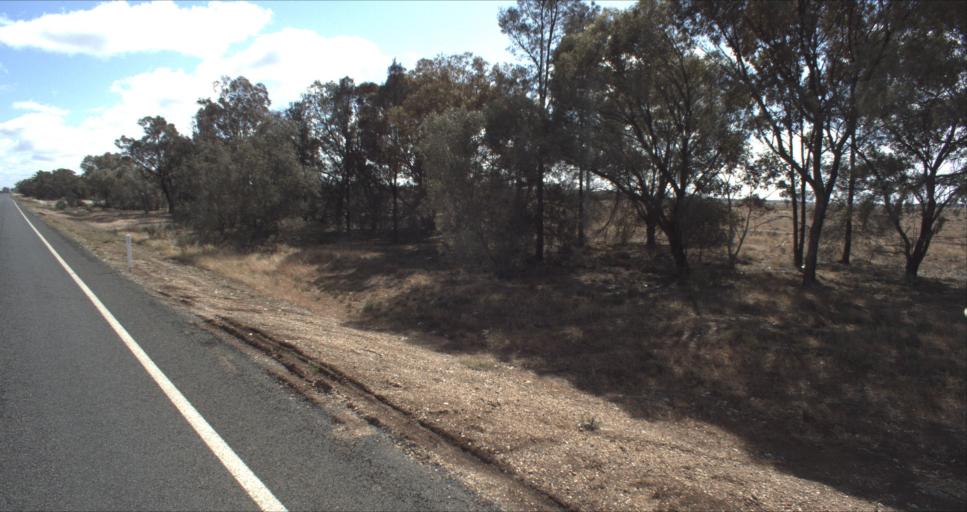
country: AU
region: New South Wales
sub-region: Murrumbidgee Shire
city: Darlington Point
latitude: -34.5279
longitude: 146.1745
